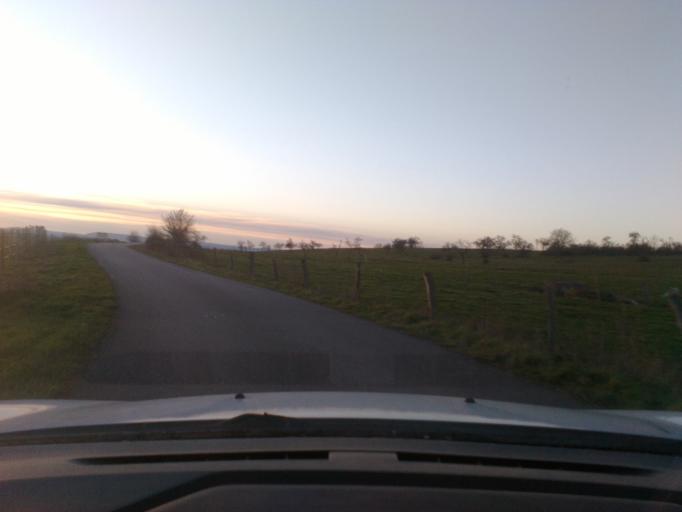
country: FR
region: Lorraine
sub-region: Departement des Vosges
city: Vittel
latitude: 48.3116
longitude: 5.9956
